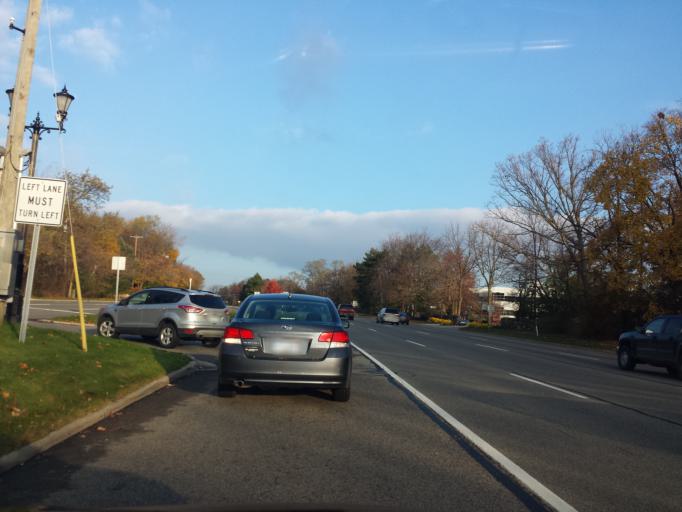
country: US
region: Michigan
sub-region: Oakland County
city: Bloomfield Hills
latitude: 42.5874
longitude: -83.2480
